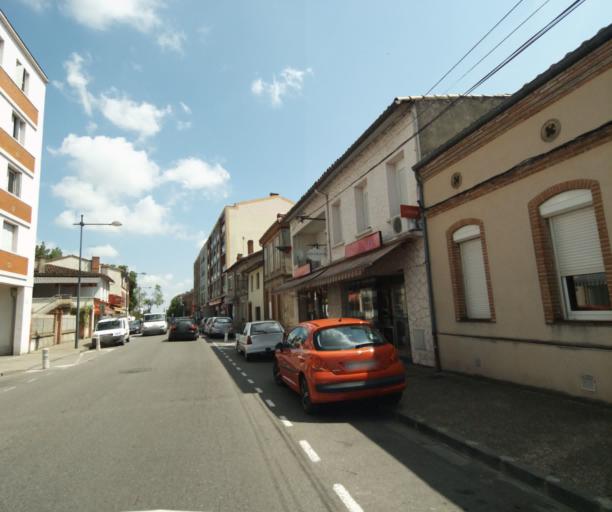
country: FR
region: Midi-Pyrenees
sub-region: Departement du Tarn-et-Garonne
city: Montauban
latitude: 44.0258
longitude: 1.3570
